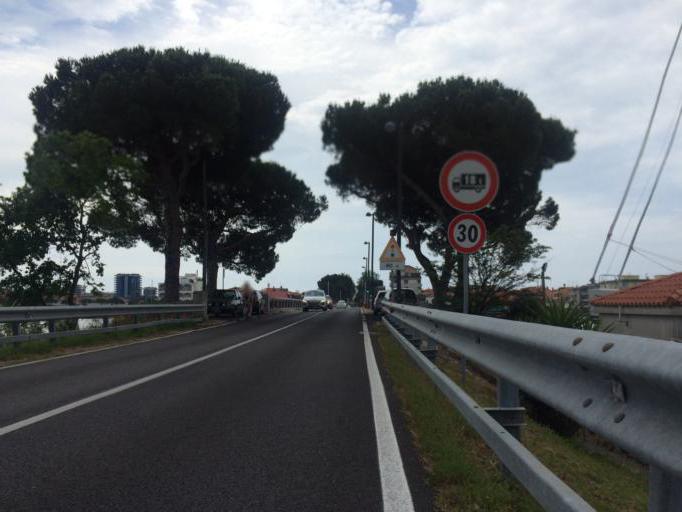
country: IT
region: Friuli Venezia Giulia
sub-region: Provincia di Gorizia
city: Grado
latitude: 45.6850
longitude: 13.3862
